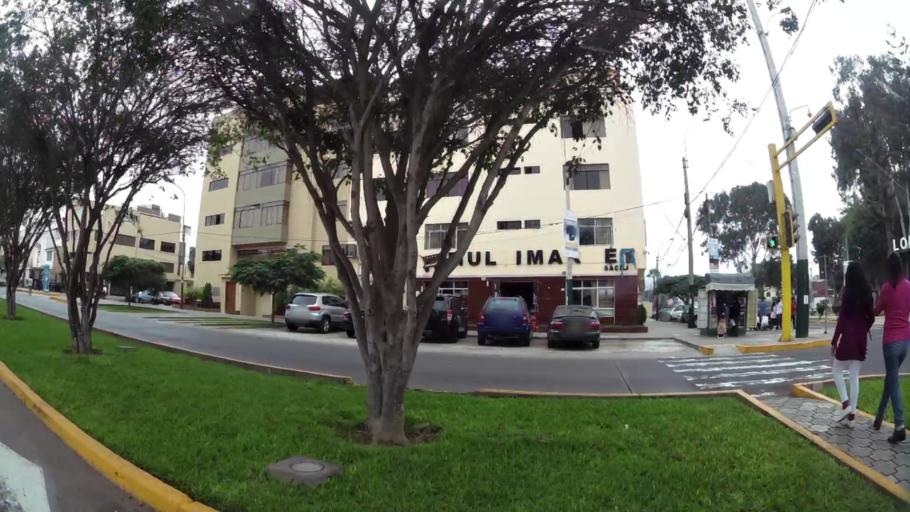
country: PE
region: Lima
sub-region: Lima
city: Surco
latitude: -12.1348
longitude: -76.9868
